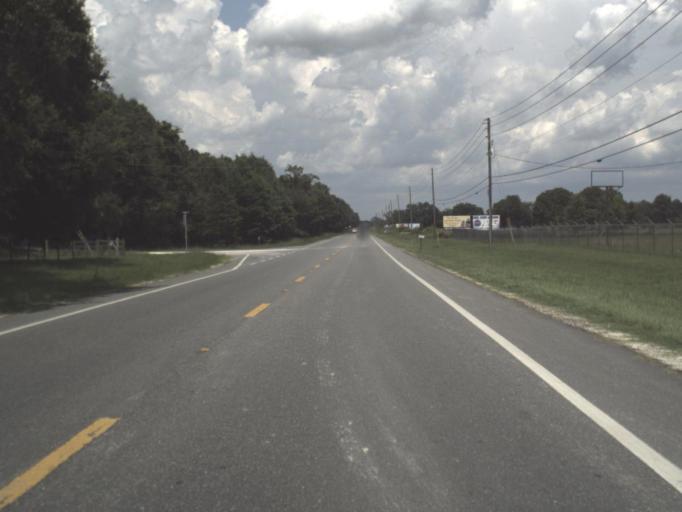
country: US
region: Florida
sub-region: Alachua County
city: Newberry
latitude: 29.6409
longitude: -82.6653
